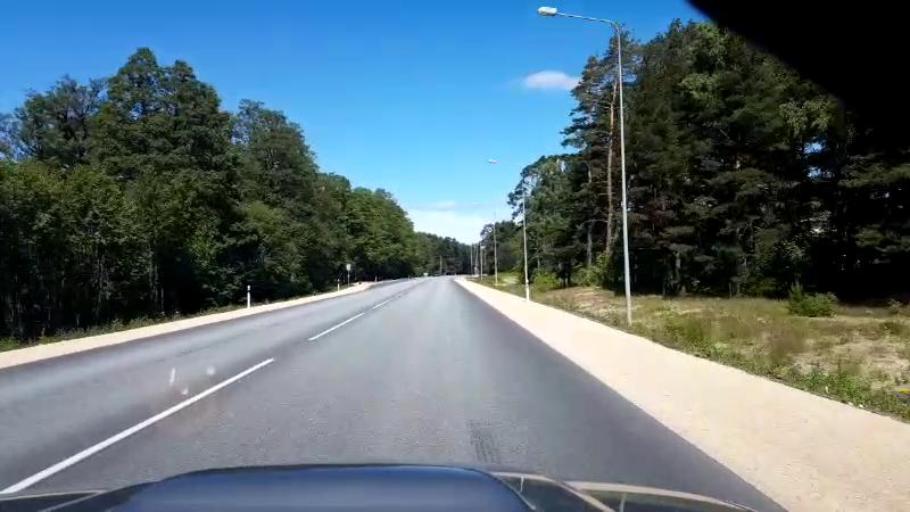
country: LV
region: Salacgrivas
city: Salacgriva
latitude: 57.7942
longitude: 24.3510
